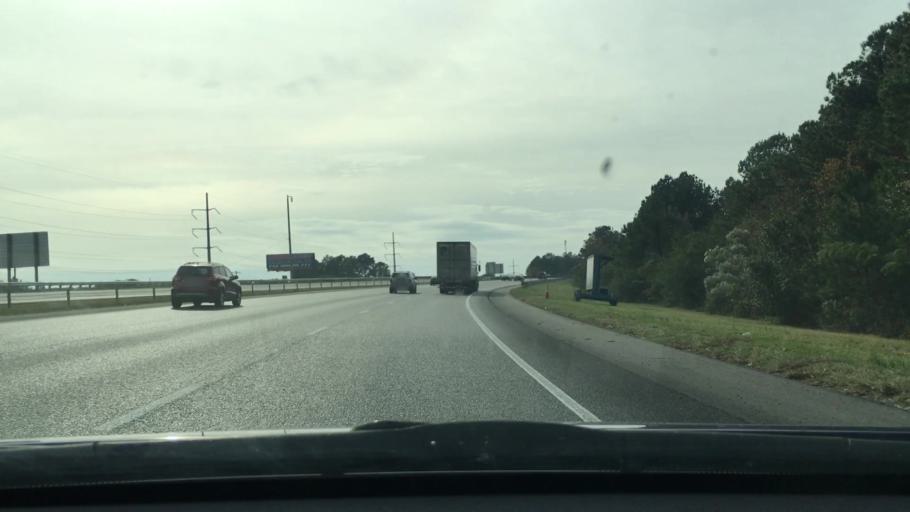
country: US
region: South Carolina
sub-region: Richland County
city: Forest Acres
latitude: 33.9563
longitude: -80.9569
